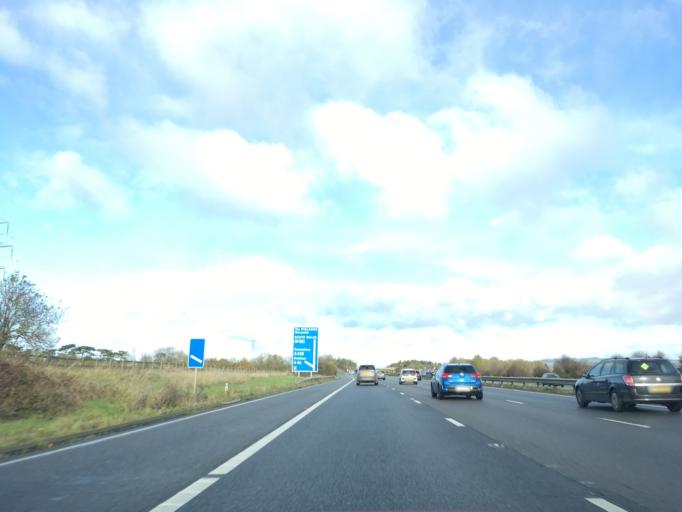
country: GB
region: England
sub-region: Gloucestershire
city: Tewkesbury
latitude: 51.9903
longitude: -2.1248
